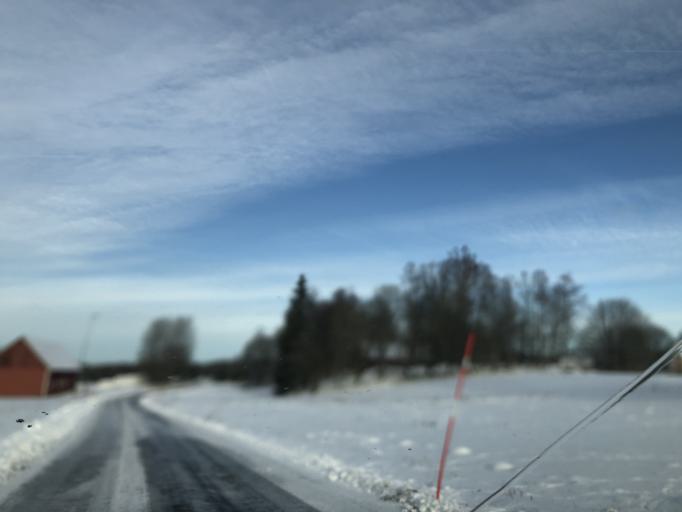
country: SE
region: Vaestra Goetaland
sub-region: Ulricehamns Kommun
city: Ulricehamn
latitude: 57.7940
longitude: 13.5344
